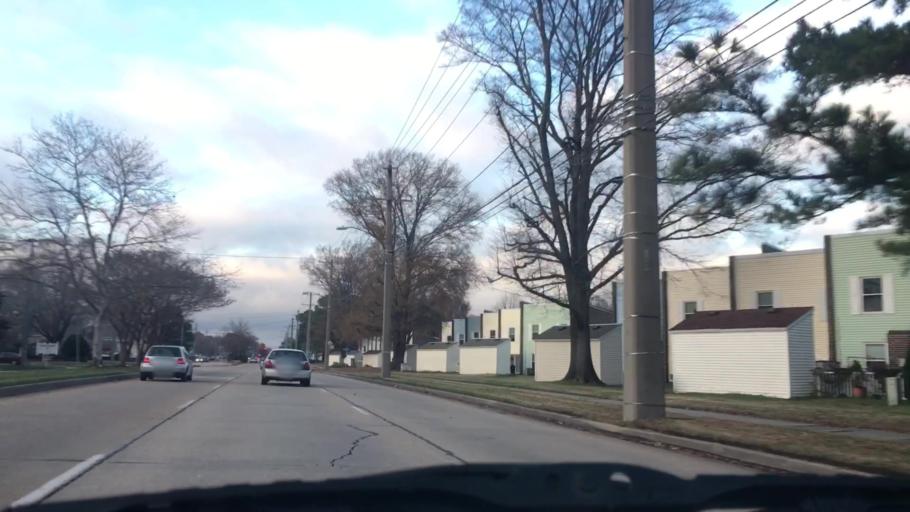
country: US
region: Virginia
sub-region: City of Norfolk
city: Norfolk
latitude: 36.9102
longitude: -76.2407
